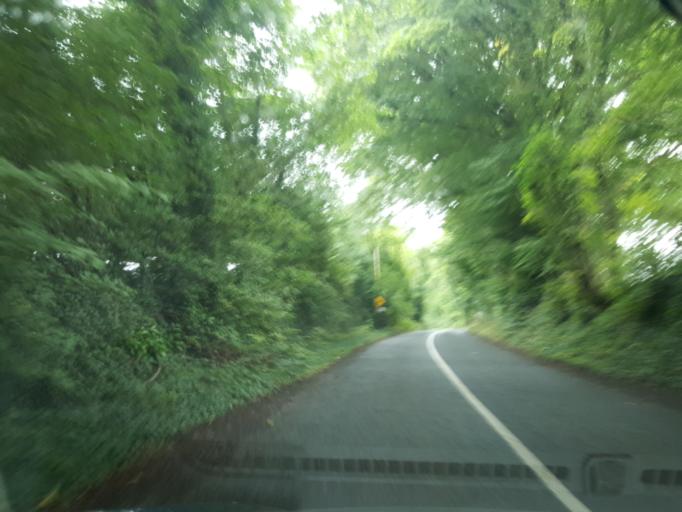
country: IE
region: Leinster
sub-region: Kildare
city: Kilcullen
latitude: 53.1206
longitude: -6.6724
